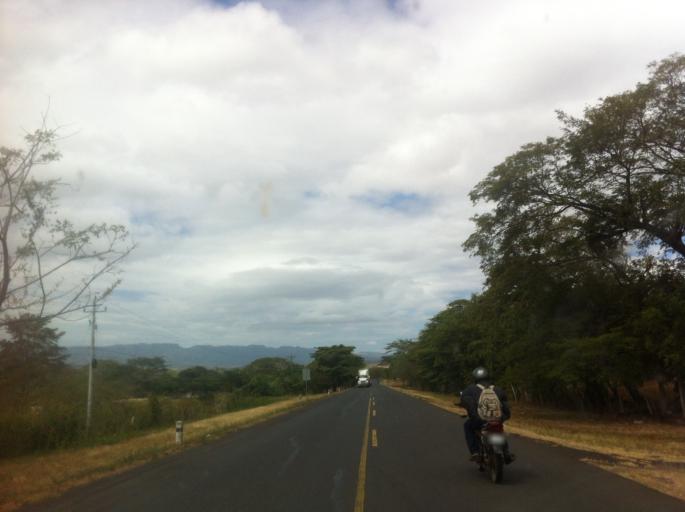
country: NI
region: Chontales
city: Juigalpa
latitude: 12.0831
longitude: -85.3299
